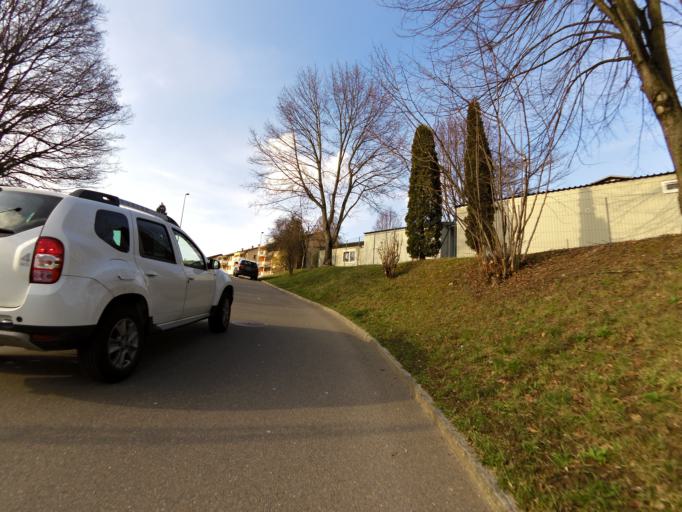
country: CH
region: Zurich
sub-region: Bezirk Dietikon
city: Oberengstringen
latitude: 47.4069
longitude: 8.4675
